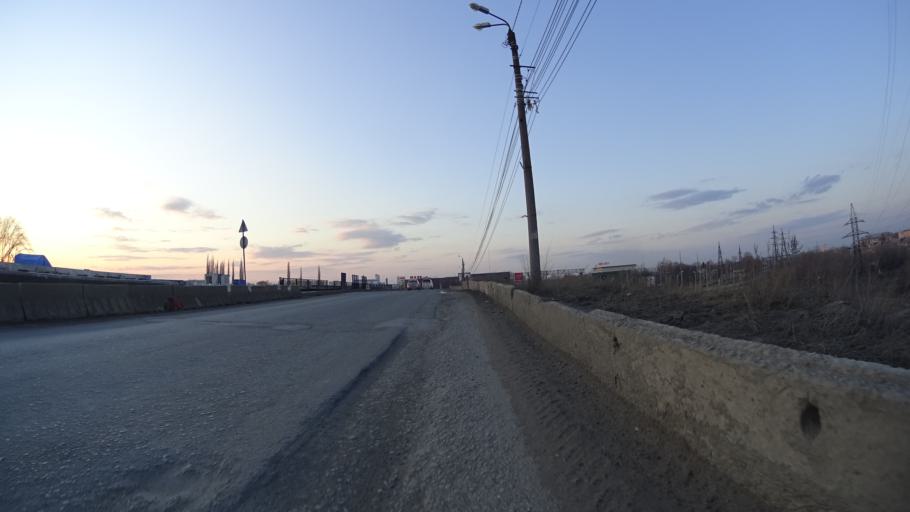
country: RU
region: Chelyabinsk
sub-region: Gorod Chelyabinsk
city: Chelyabinsk
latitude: 55.1157
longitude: 61.3858
